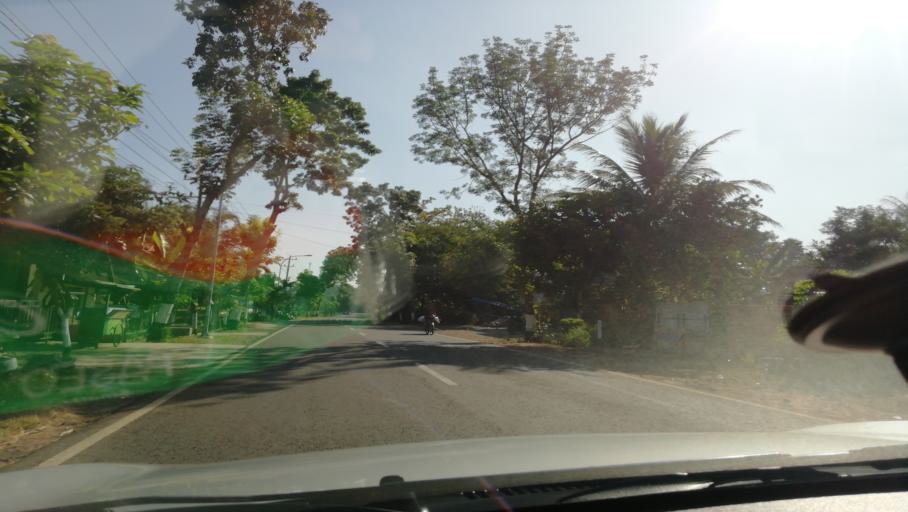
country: ID
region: Central Java
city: Kutoarjo
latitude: -7.7114
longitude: 109.9739
